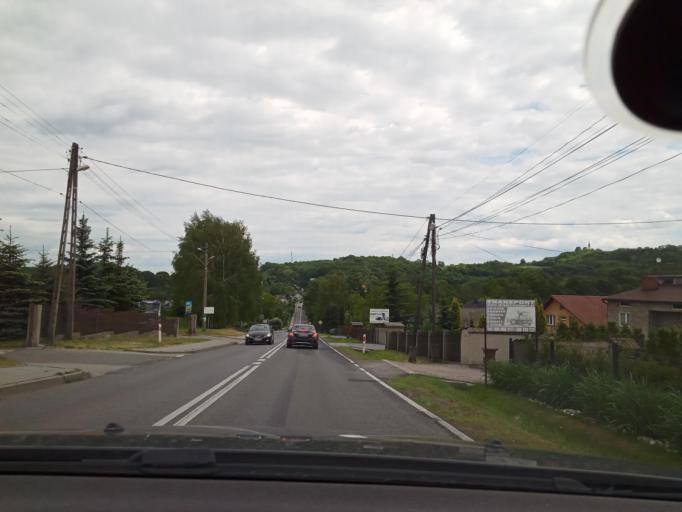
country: PL
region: Lesser Poland Voivodeship
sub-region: Powiat wielicki
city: Tomaszkowice
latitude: 49.9753
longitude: 20.1025
